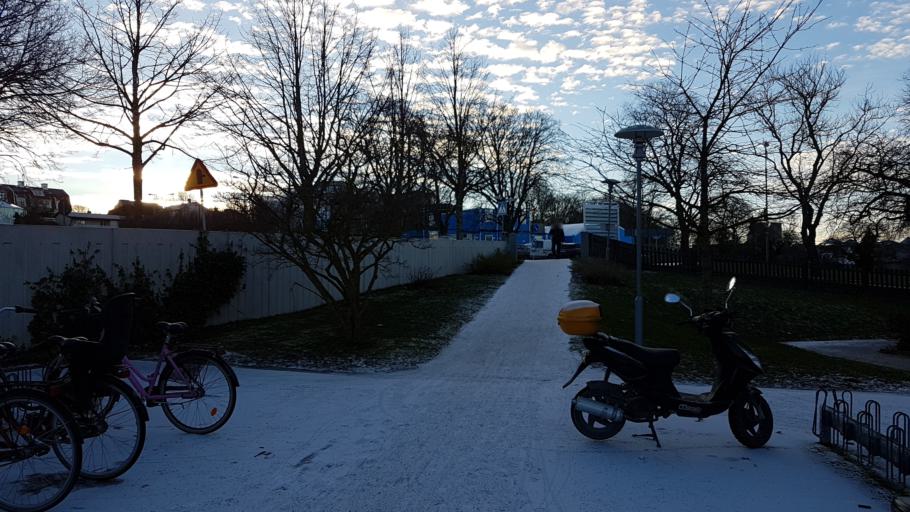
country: SE
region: Gotland
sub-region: Gotland
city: Visby
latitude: 57.6477
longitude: 18.3010
